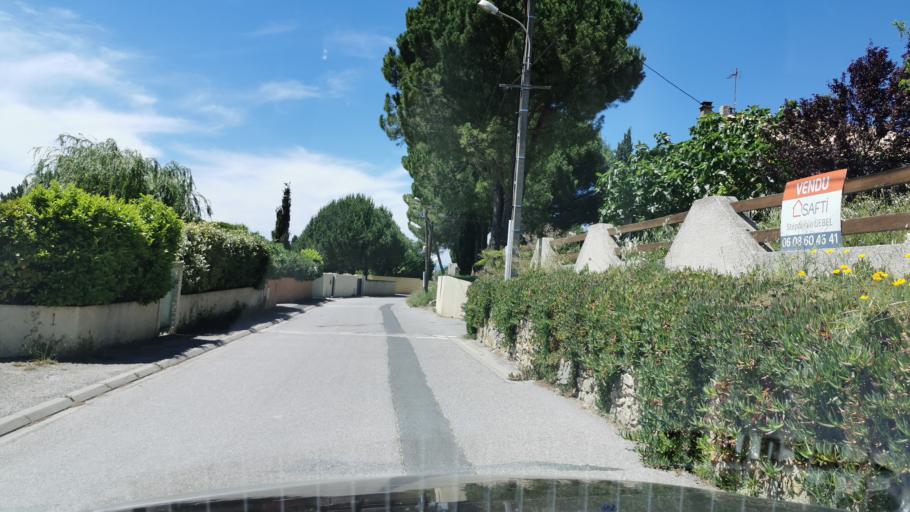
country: FR
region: Languedoc-Roussillon
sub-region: Departement de l'Aude
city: Nevian
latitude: 43.2137
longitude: 2.8999
